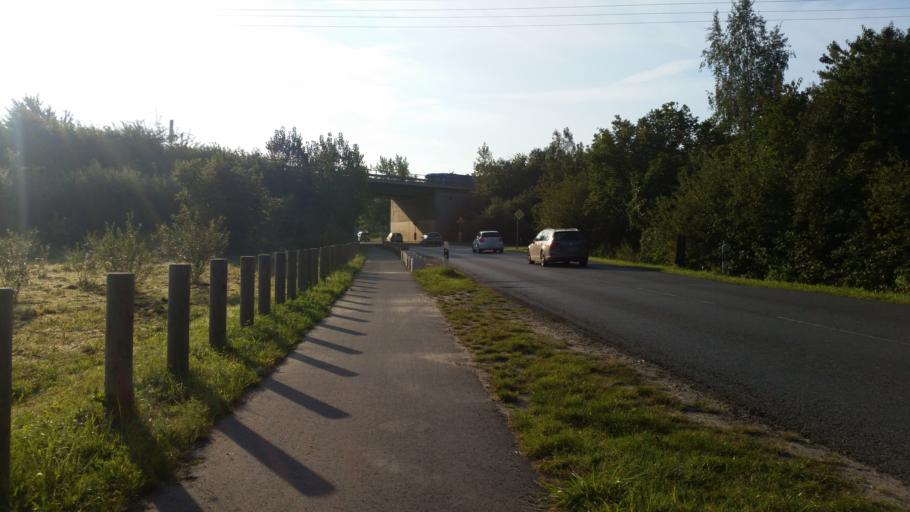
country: DE
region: Lower Saxony
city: Weyhausen
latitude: 52.4301
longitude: 10.7369
